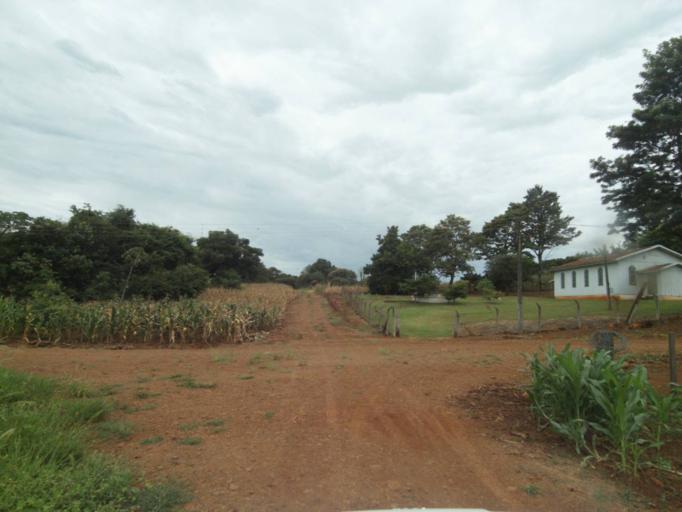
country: BR
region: Parana
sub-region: Guaraniacu
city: Guaraniacu
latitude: -24.9202
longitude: -52.9365
